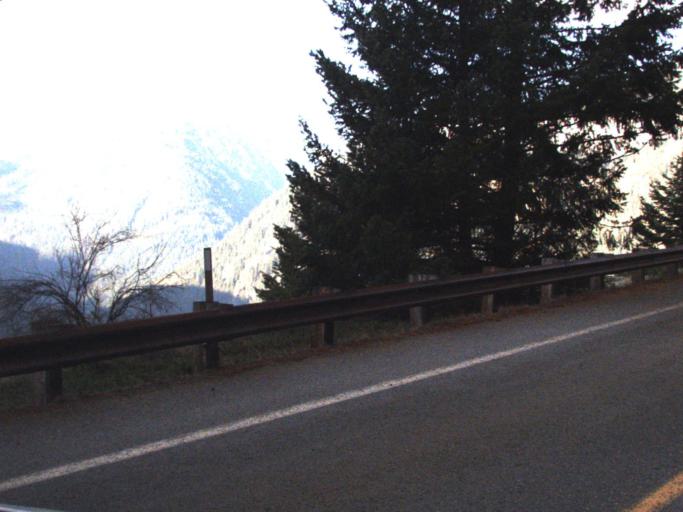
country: US
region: Washington
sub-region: Snohomish County
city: Darrington
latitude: 48.7082
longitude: -121.0964
